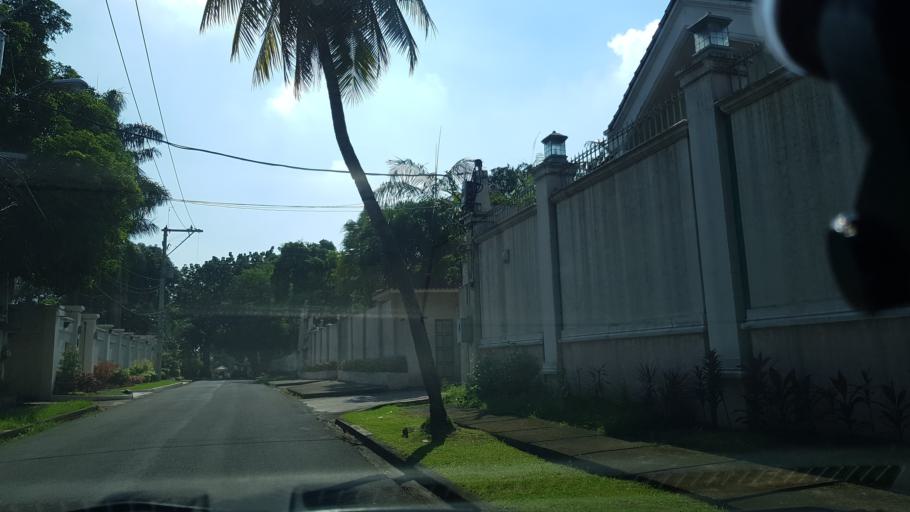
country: PH
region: Metro Manila
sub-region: San Juan
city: San Juan
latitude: 14.6177
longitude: 121.0286
